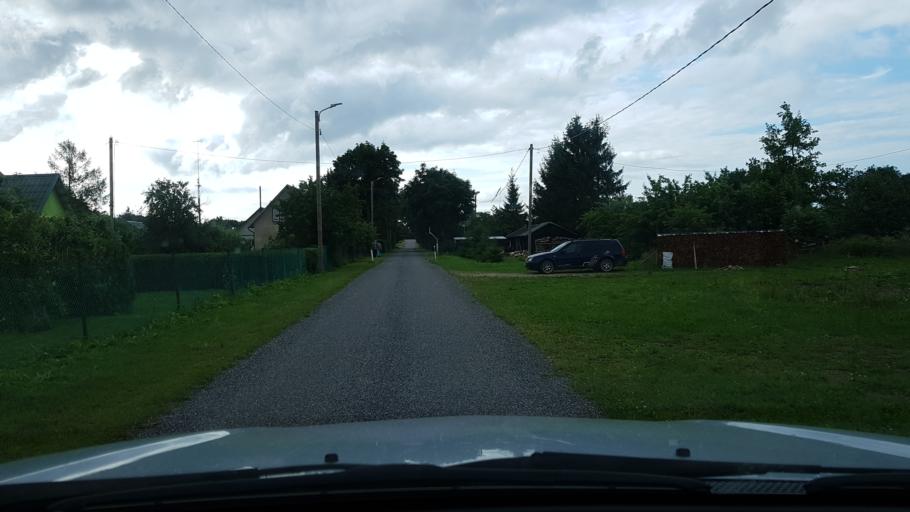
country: EE
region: Ida-Virumaa
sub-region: Narva-Joesuu linn
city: Narva-Joesuu
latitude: 59.3916
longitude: 27.9761
